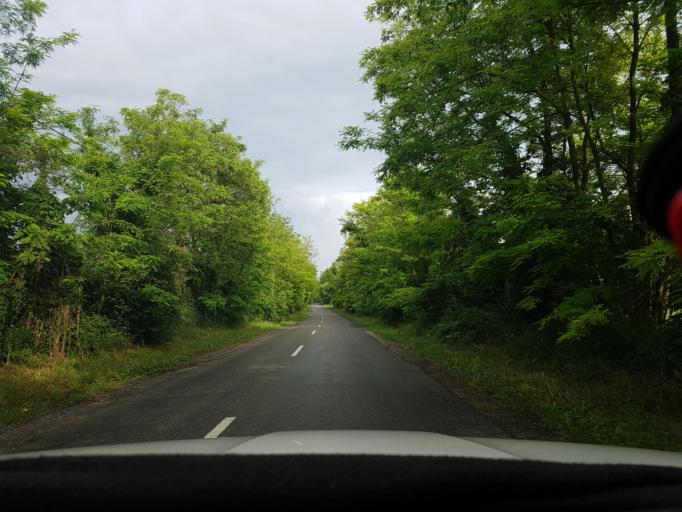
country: HU
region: Komarom-Esztergom
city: Nyergesujfalu
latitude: 47.7155
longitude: 18.5686
